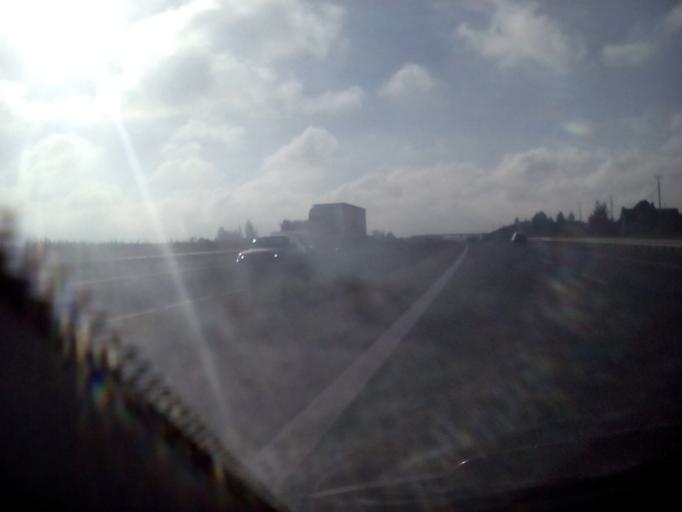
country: PL
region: Masovian Voivodeship
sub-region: Powiat grojecki
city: Jasieniec
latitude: 51.7758
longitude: 20.8976
